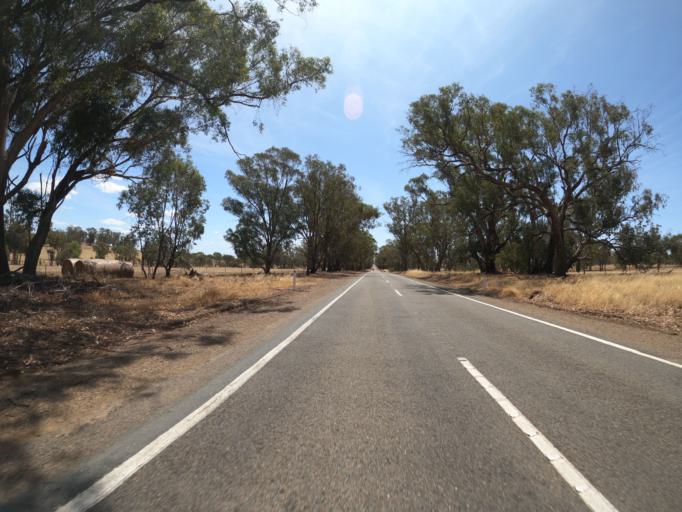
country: AU
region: Victoria
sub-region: Benalla
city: Benalla
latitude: -36.3611
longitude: 145.9677
